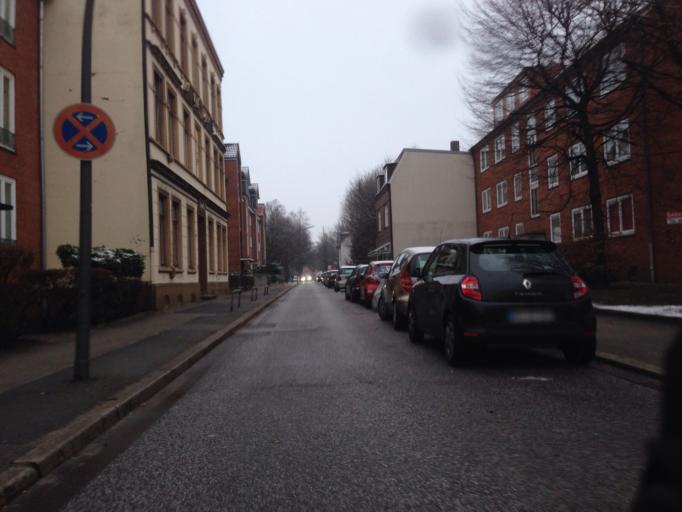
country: DE
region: Hamburg
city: Marienthal
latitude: 53.5778
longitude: 10.0675
